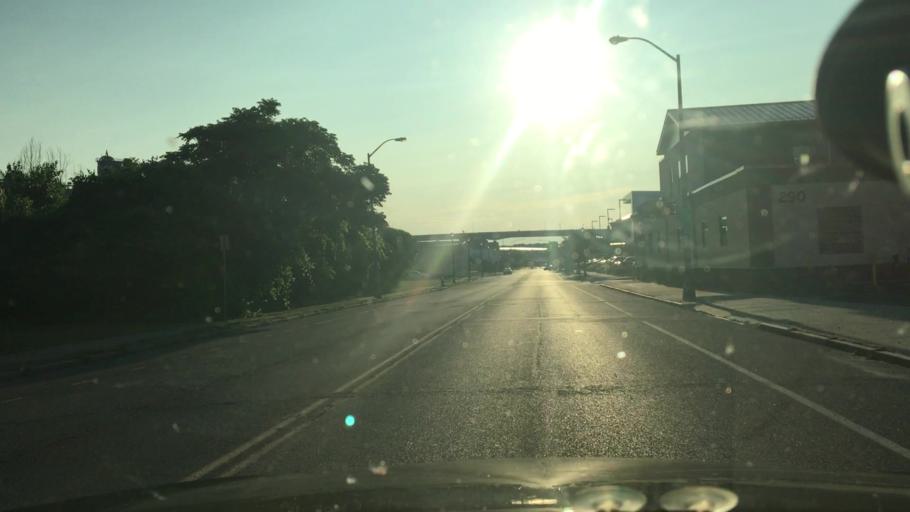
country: US
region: New York
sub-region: Erie County
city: Buffalo
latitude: 42.8724
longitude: -78.8683
